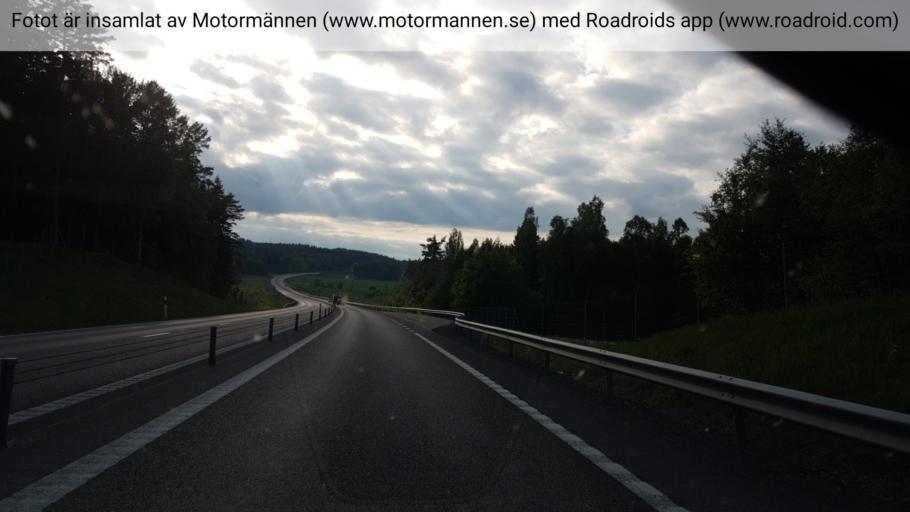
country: SE
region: Joenkoeping
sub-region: Jonkopings Kommun
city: Tenhult
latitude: 57.7194
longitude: 14.3730
